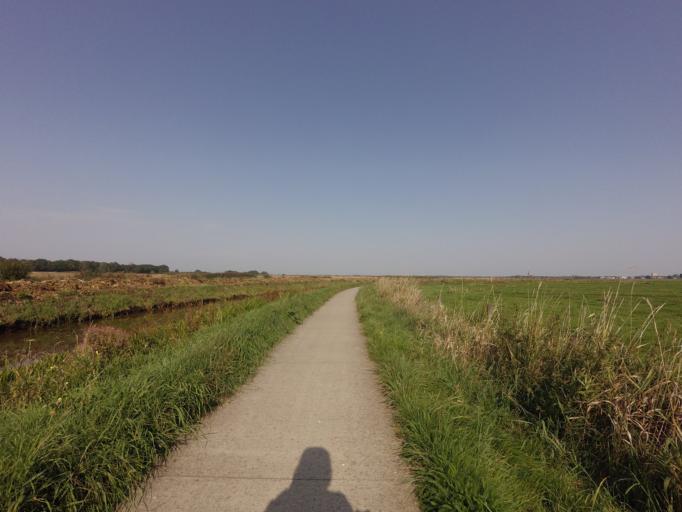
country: NL
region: Groningen
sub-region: Gemeente Groningen
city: Groningen
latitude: 53.1565
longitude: 6.5375
